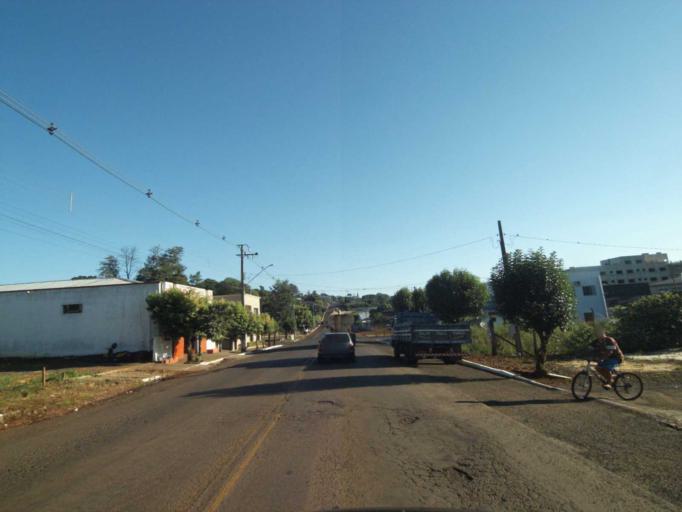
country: BR
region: Parana
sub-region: Coronel Vivida
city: Coronel Vivida
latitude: -25.9654
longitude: -52.8136
